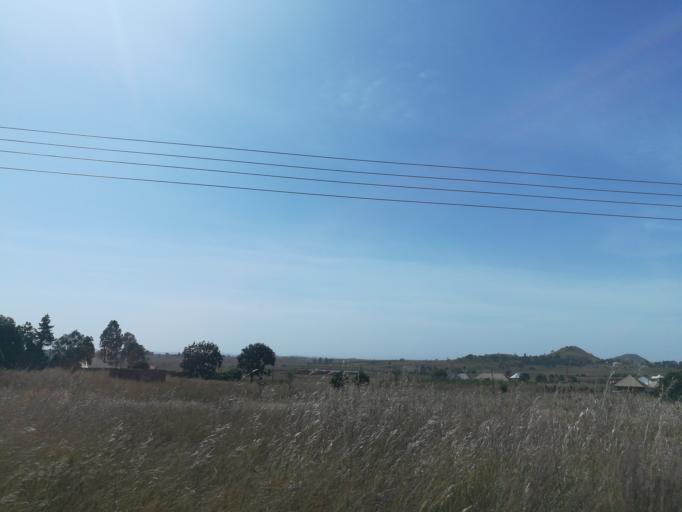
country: NG
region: Plateau
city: Bukuru
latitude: 9.7740
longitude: 8.9179
